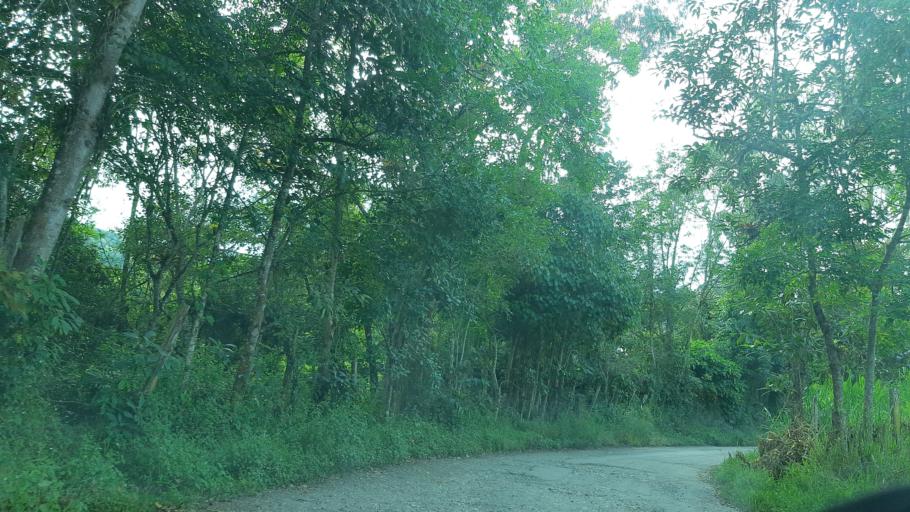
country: CO
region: Cundinamarca
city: Tenza
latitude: 5.0440
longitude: -73.4223
